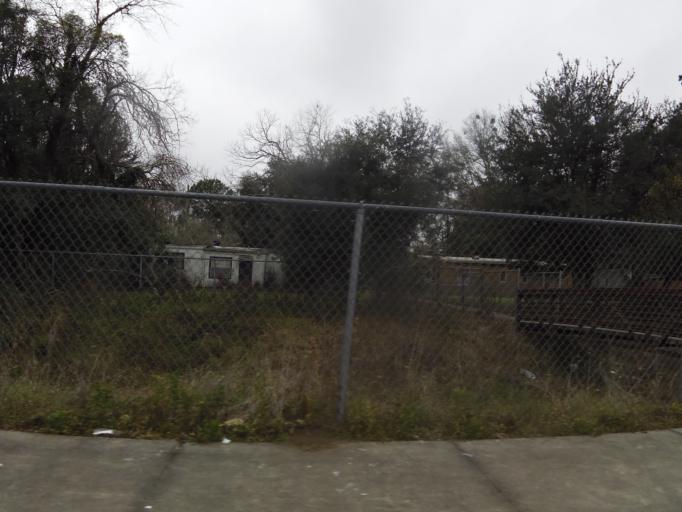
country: US
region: Florida
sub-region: Duval County
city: Jacksonville
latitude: 30.3779
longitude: -81.7015
